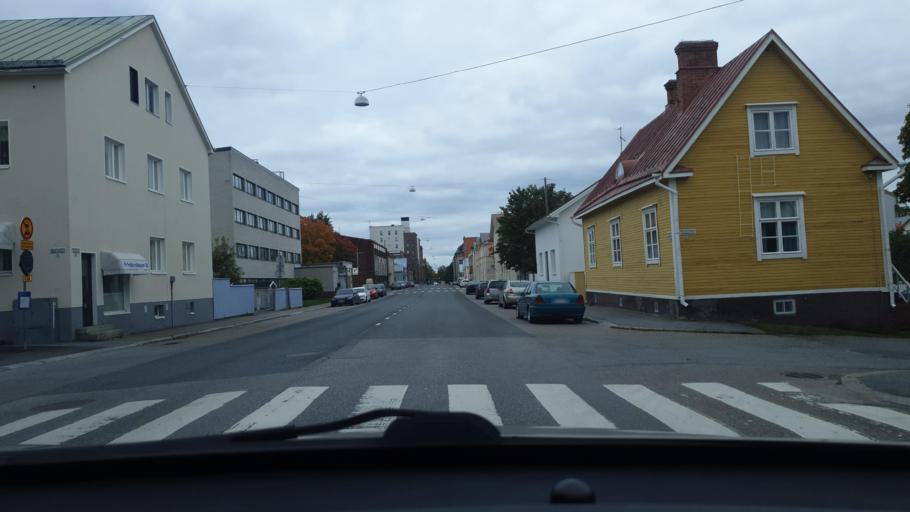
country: FI
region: Ostrobothnia
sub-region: Vaasa
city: Vaasa
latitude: 63.0924
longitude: 21.6255
